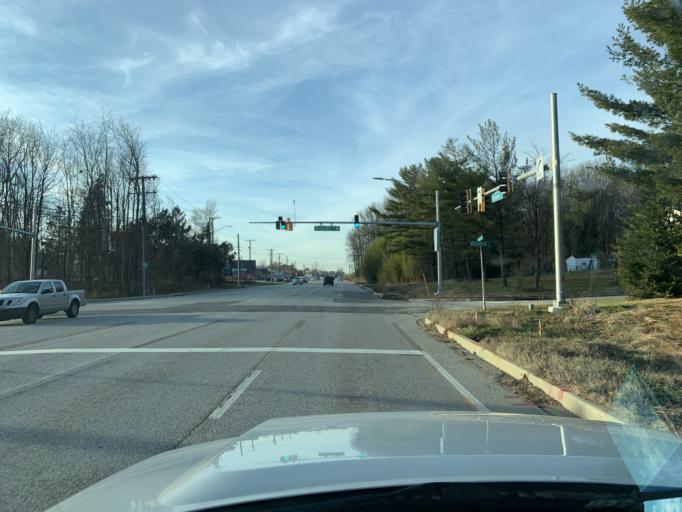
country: US
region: Maryland
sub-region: Anne Arundel County
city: Fort Meade
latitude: 39.1356
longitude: -76.7473
